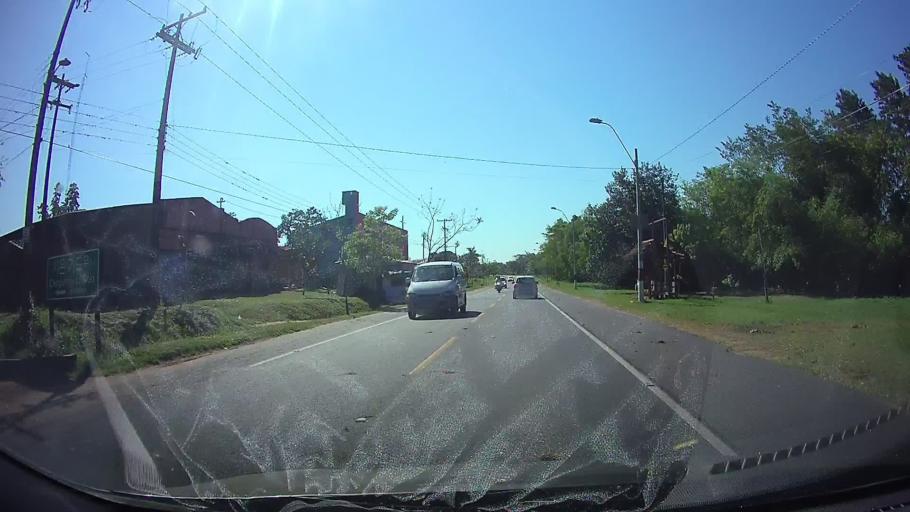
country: PY
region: Central
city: Aregua
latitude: -25.3282
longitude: -57.3604
